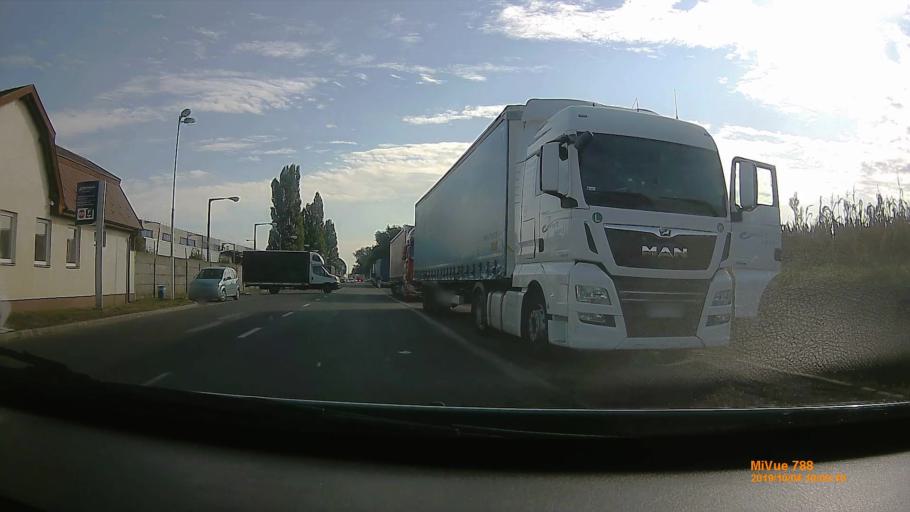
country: HU
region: Szabolcs-Szatmar-Bereg
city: Nyiregyhaza
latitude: 47.9418
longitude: 21.6837
